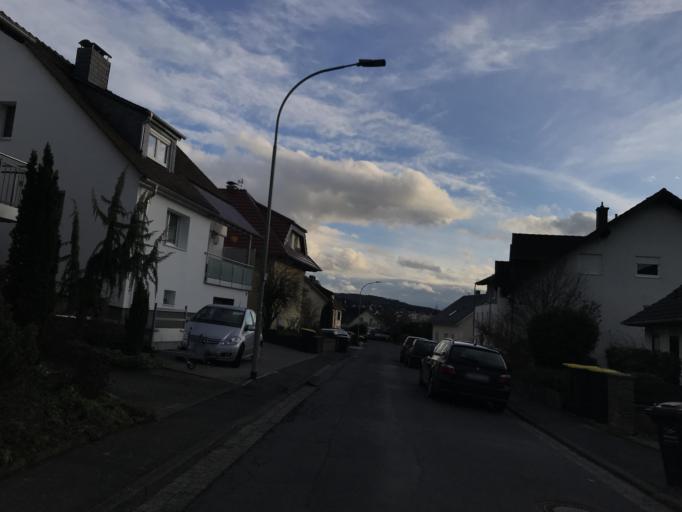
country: BE
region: Wallonia
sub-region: Province du Brabant Wallon
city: Tubize
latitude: 50.6686
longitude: 4.1684
